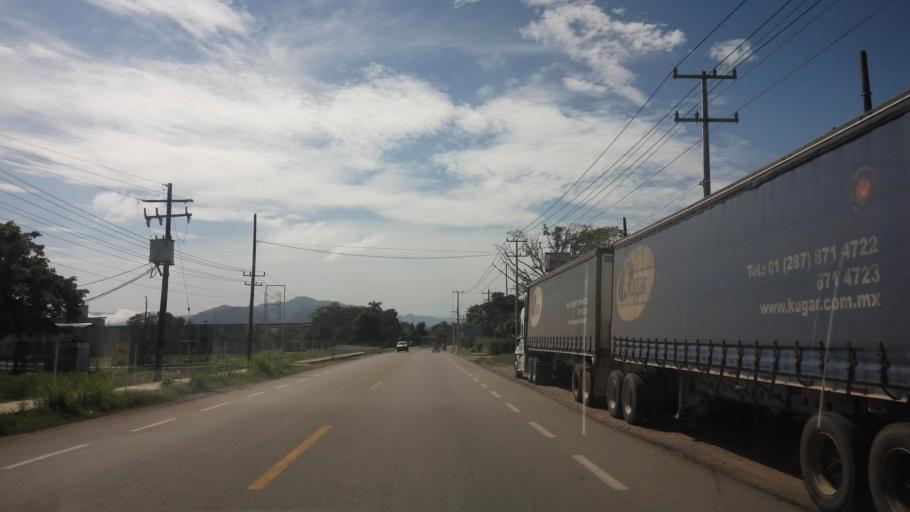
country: MX
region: Tabasco
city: Teapa
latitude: 17.5723
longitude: -92.9570
